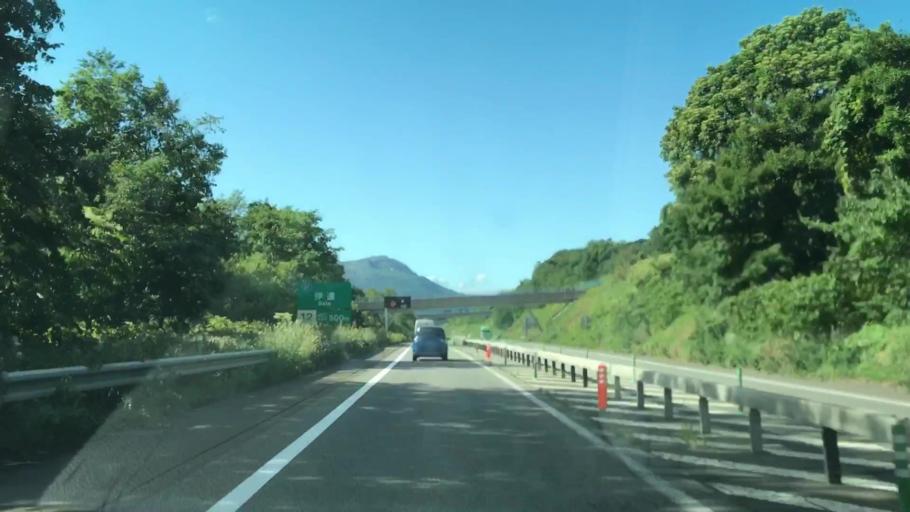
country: JP
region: Hokkaido
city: Date
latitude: 42.4753
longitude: 140.9028
